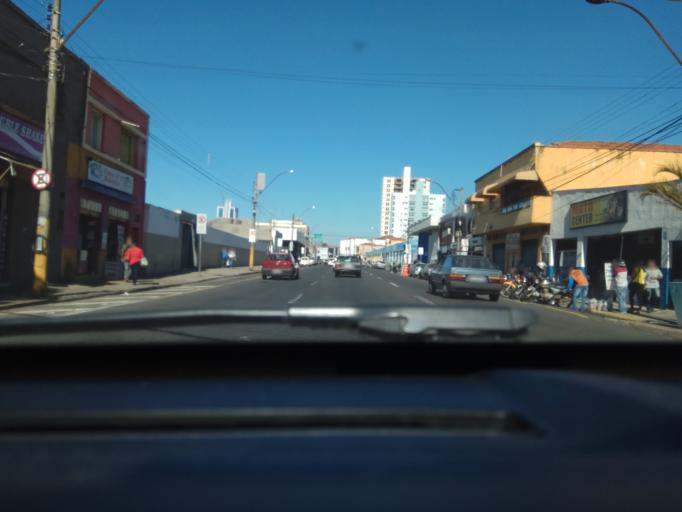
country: BR
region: Sao Paulo
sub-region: Piracicaba
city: Piracicaba
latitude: -22.7282
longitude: -47.6474
